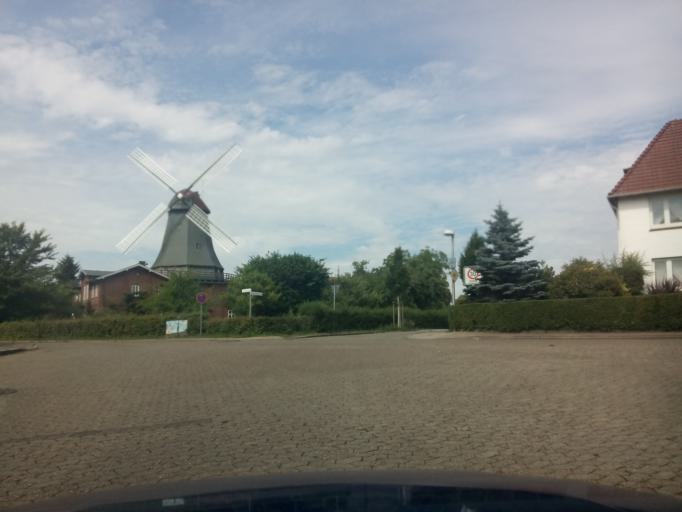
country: DE
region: Lower Saxony
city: Osterholz-Scharmbeck
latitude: 53.2288
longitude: 8.7905
